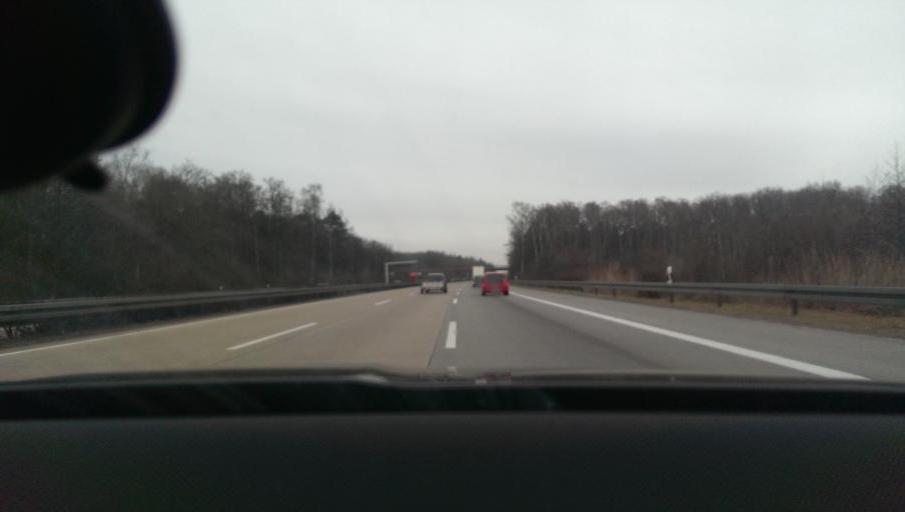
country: DE
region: Lower Saxony
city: Isernhagen Farster Bauerschaft
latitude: 52.4544
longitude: 9.8608
